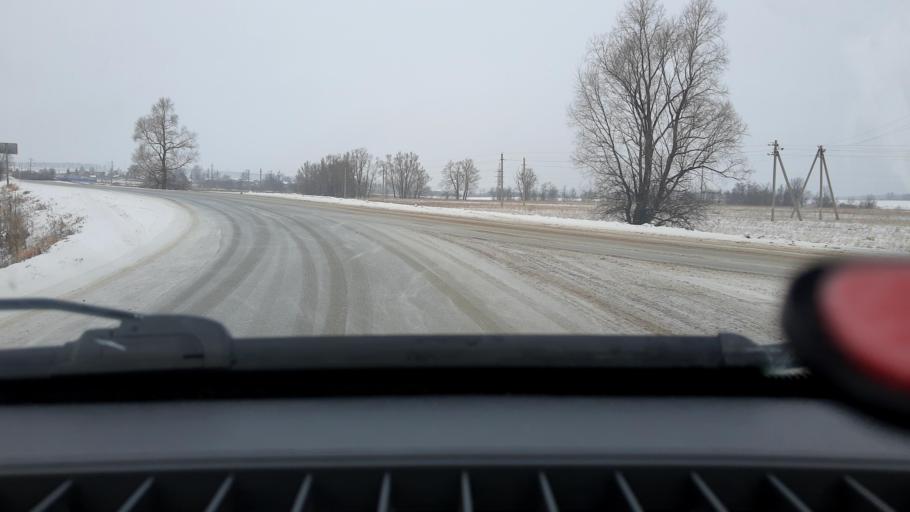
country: RU
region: Bashkortostan
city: Iglino
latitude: 54.7271
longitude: 56.4057
